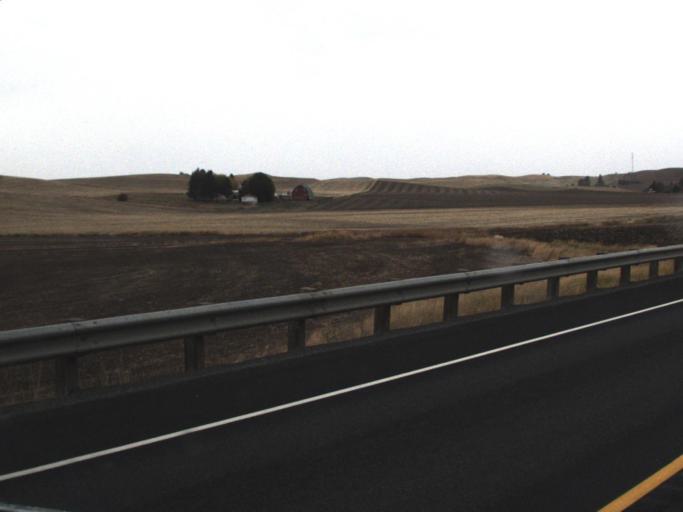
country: US
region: Washington
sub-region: Whitman County
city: Pullman
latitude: 46.7763
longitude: -117.2841
